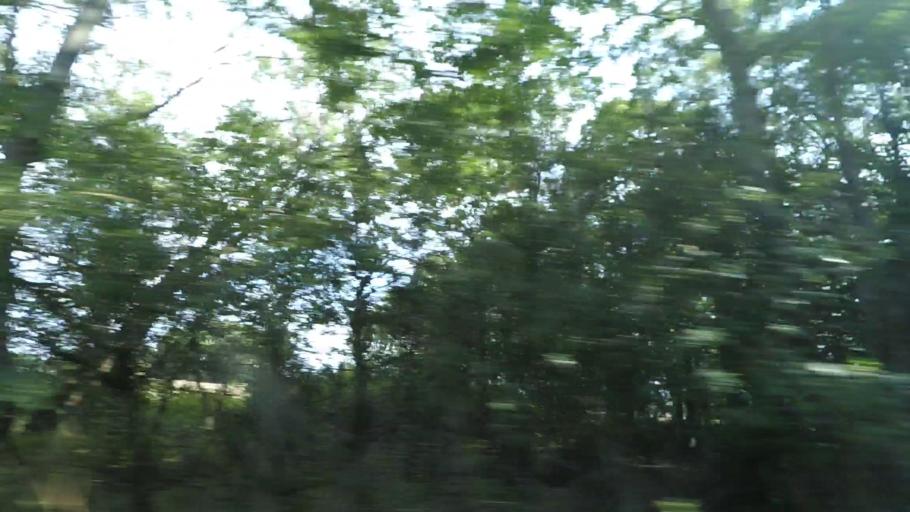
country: DK
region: Central Jutland
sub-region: Syddjurs Kommune
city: Ryomgard
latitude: 56.4668
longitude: 10.5159
